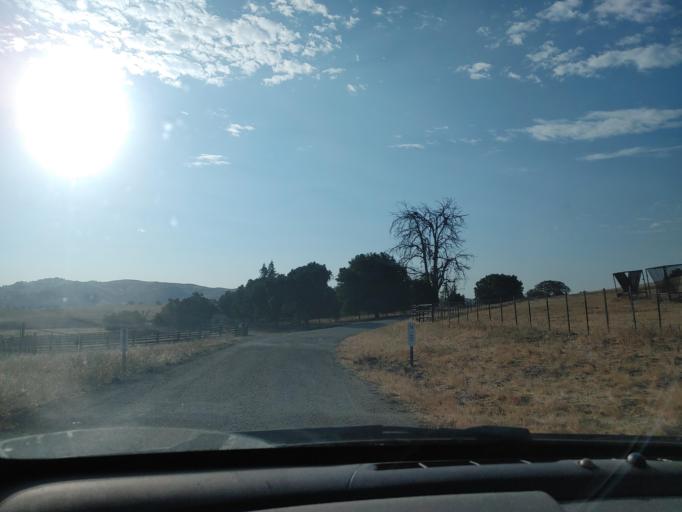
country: US
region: California
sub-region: San Benito County
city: Ridgemark
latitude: 36.7677
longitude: -121.1851
